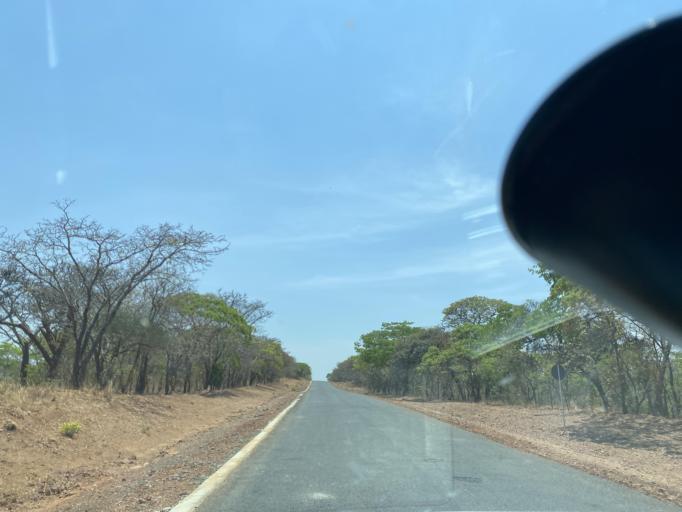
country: ZM
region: Lusaka
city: Kafue
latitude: -15.8525
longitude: 28.4182
